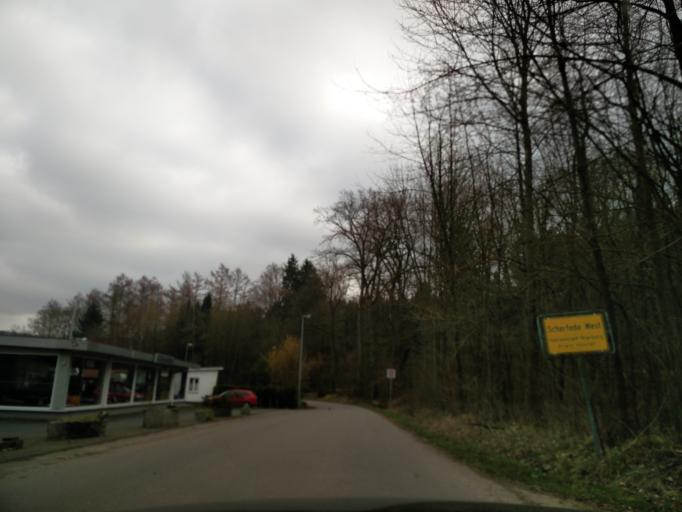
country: DE
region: North Rhine-Westphalia
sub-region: Regierungsbezirk Detmold
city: Willebadessen
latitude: 51.5217
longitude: 9.0049
